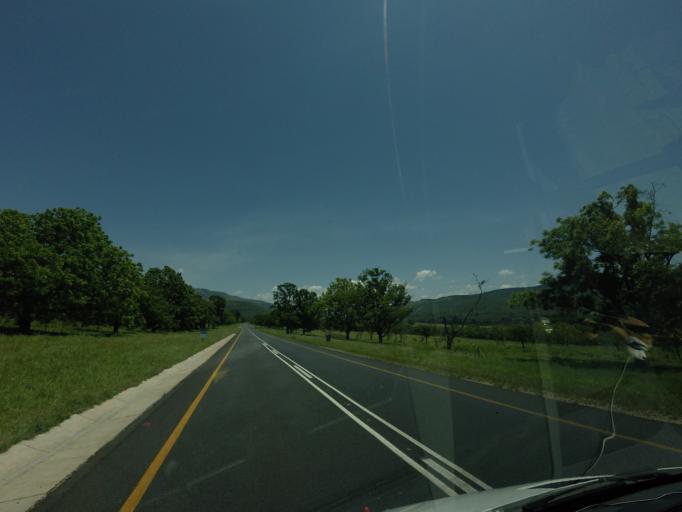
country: ZA
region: Mpumalanga
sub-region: Ehlanzeni District
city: Nelspruit
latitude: -25.4540
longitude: 30.6717
